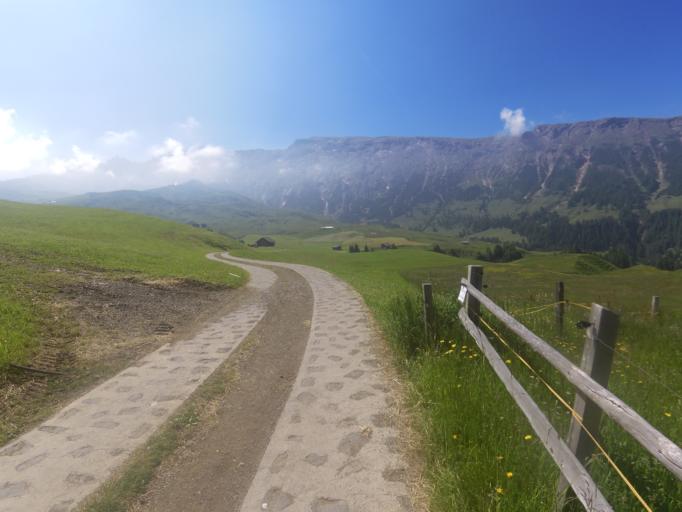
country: IT
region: Trentino-Alto Adige
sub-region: Bolzano
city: Siusi
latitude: 46.5222
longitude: 11.6090
